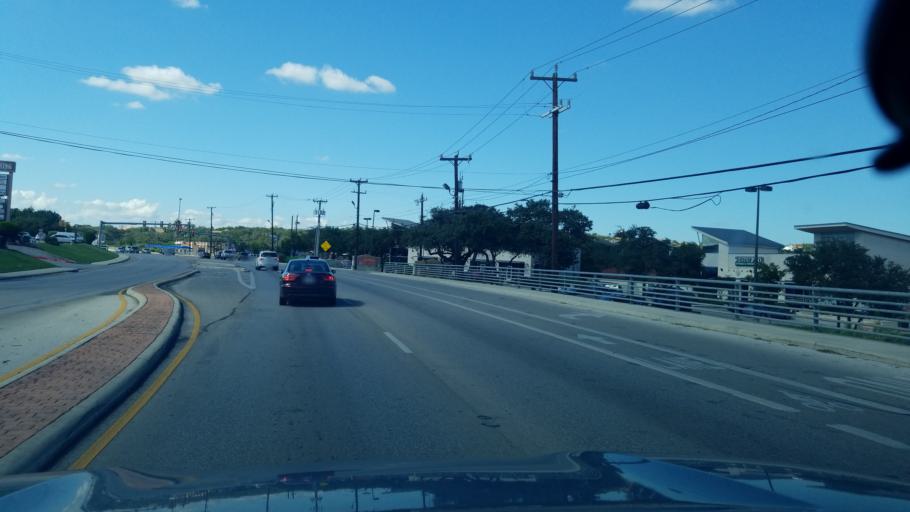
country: US
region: Texas
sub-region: Bexar County
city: Hollywood Park
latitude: 29.6199
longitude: -98.5118
